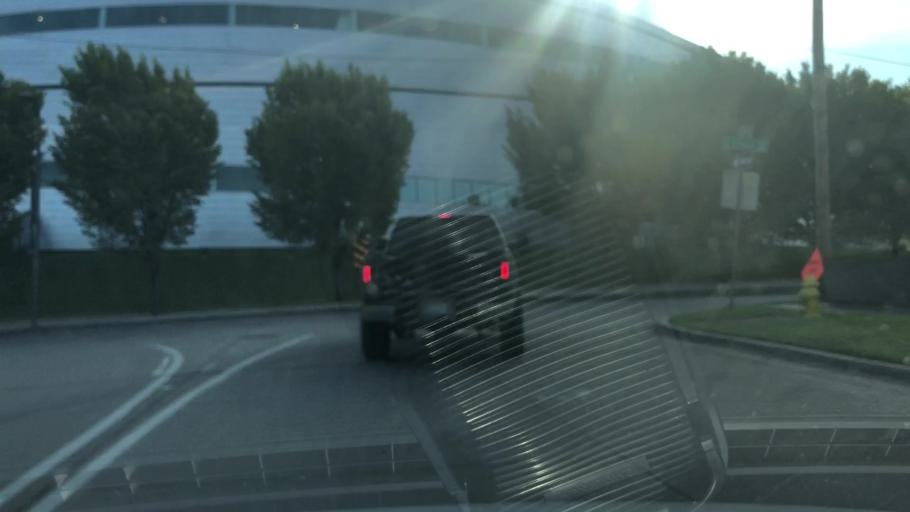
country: US
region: Oklahoma
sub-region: Tulsa County
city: Tulsa
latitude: 36.1524
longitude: -95.9979
